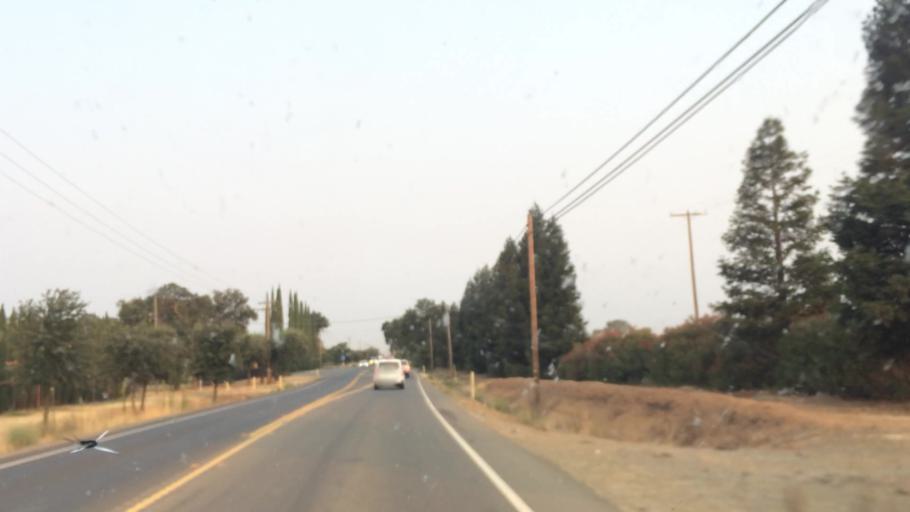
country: US
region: California
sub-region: Sacramento County
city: Rosemont
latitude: 38.5263
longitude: -121.3247
